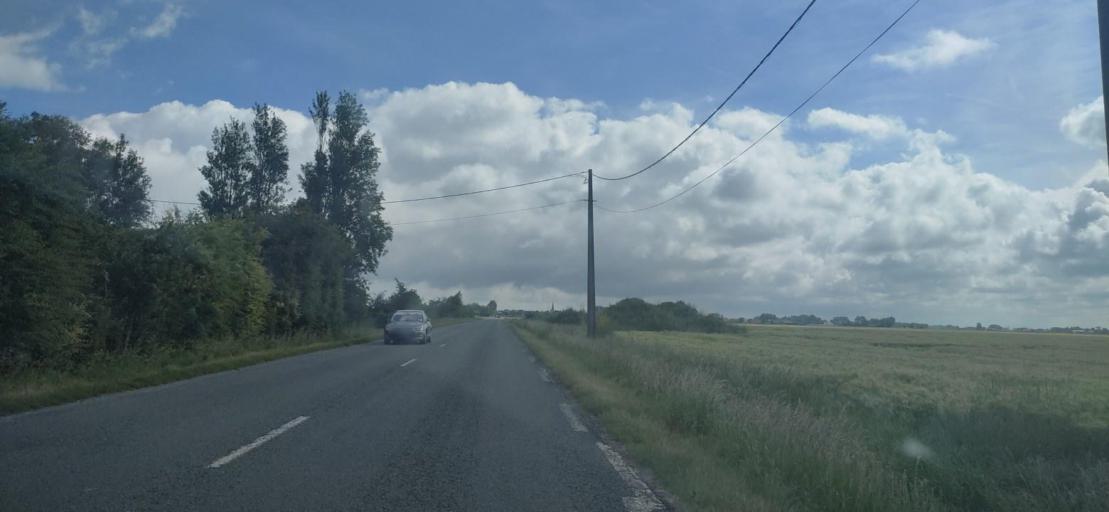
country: FR
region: Nord-Pas-de-Calais
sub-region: Departement du Pas-de-Calais
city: Oye-Plage
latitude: 50.9691
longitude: 2.0184
